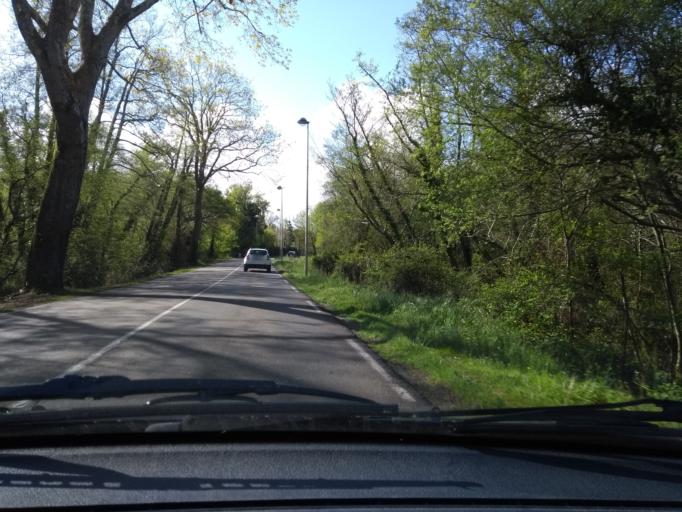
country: FR
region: Aquitaine
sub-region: Departement des Landes
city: Parentis-en-Born
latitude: 44.3424
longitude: -1.0814
